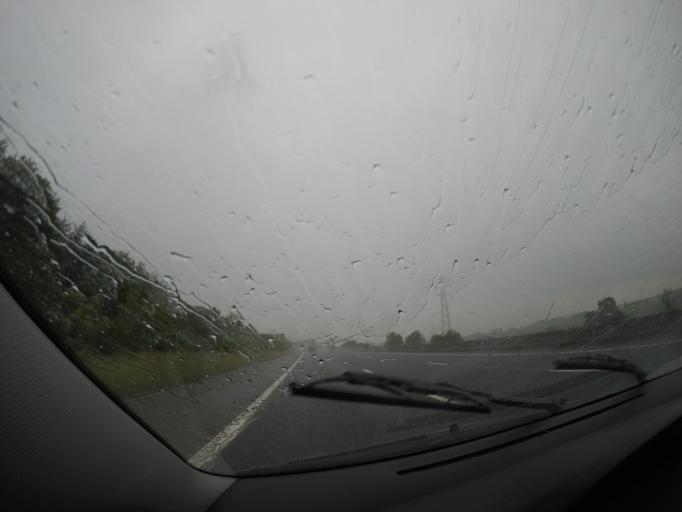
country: GB
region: England
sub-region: Cumbria
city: Penrith
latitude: 54.6750
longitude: -2.7789
